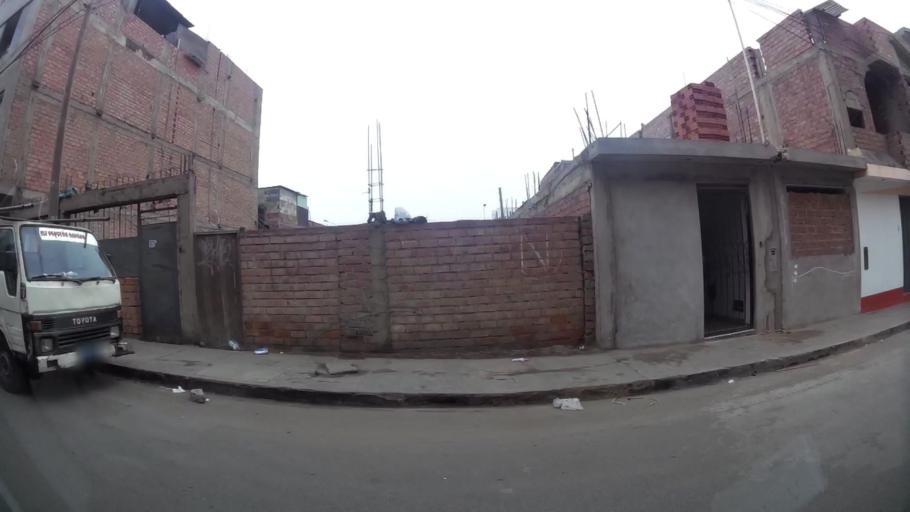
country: PE
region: Lima
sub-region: Lima
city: Surco
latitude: -12.1602
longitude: -76.9765
